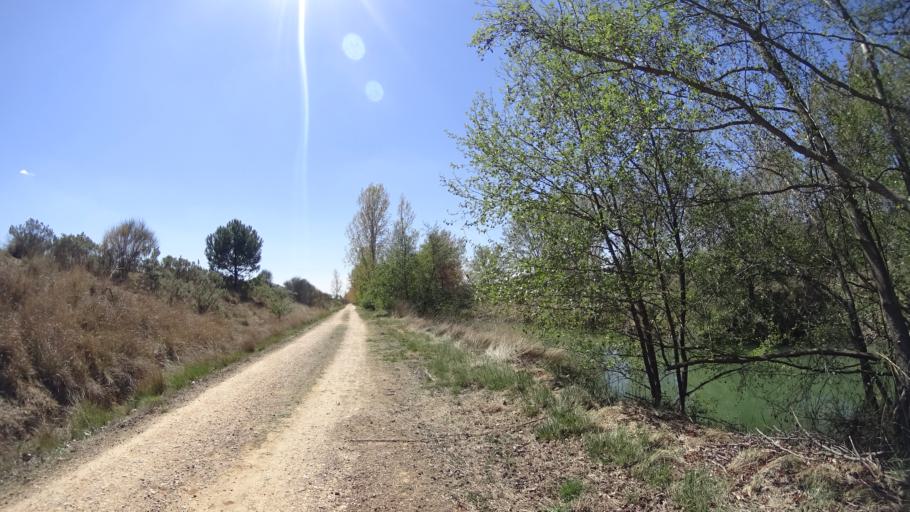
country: ES
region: Castille and Leon
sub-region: Provincia de Valladolid
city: Cubillas de Santa Marta
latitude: 41.7851
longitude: -4.6065
